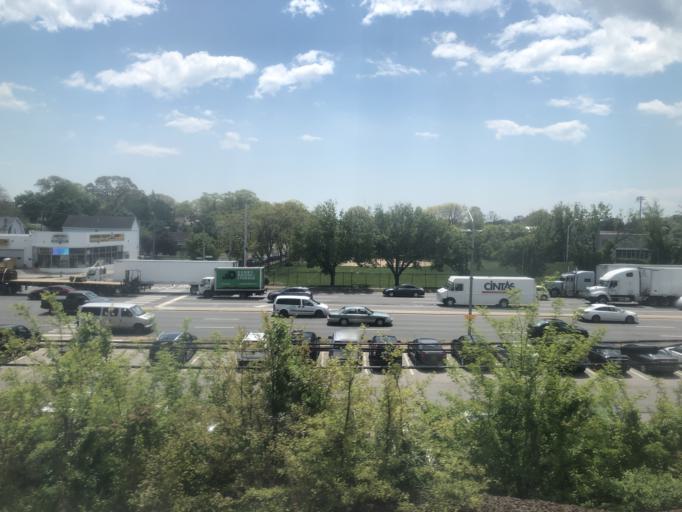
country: US
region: New York
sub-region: Nassau County
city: Baldwin
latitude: 40.6566
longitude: -73.6014
